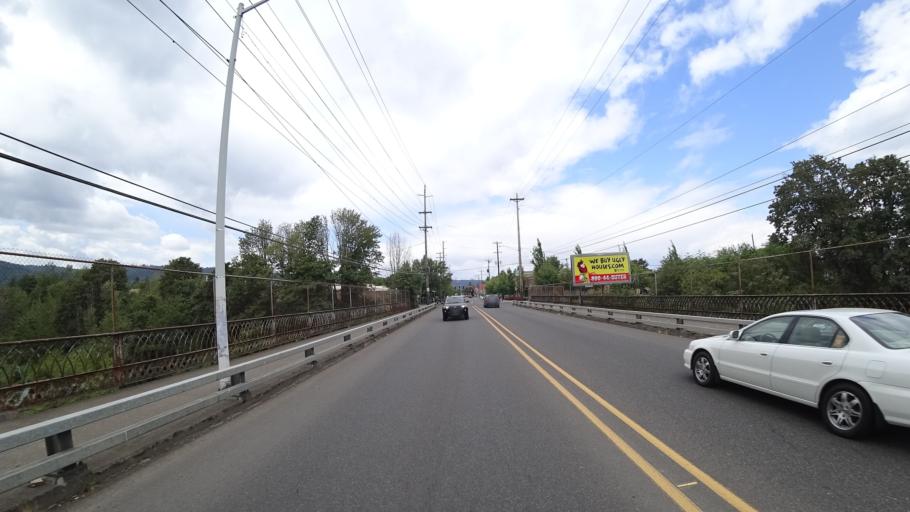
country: US
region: Oregon
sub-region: Washington County
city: West Haven
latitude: 45.5863
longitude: -122.7358
